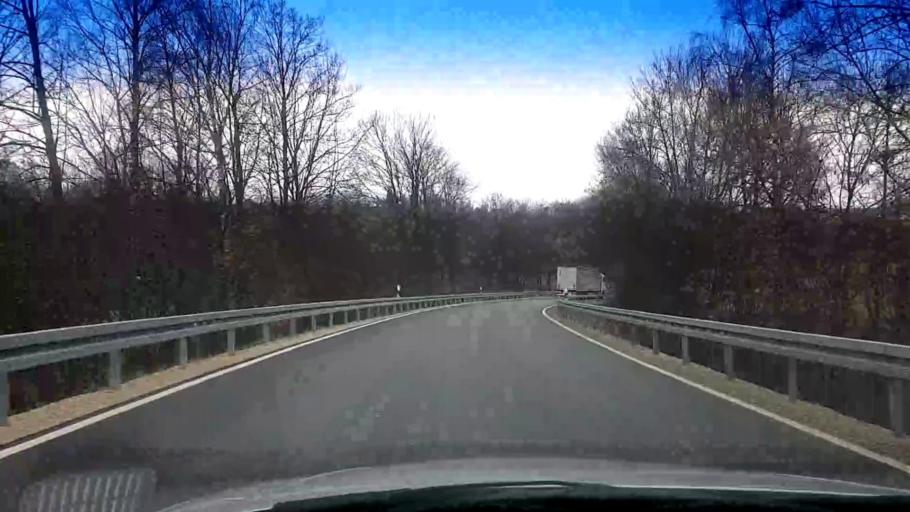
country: DE
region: Bavaria
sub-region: Upper Franconia
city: Kulmbach
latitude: 50.1071
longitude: 11.4320
